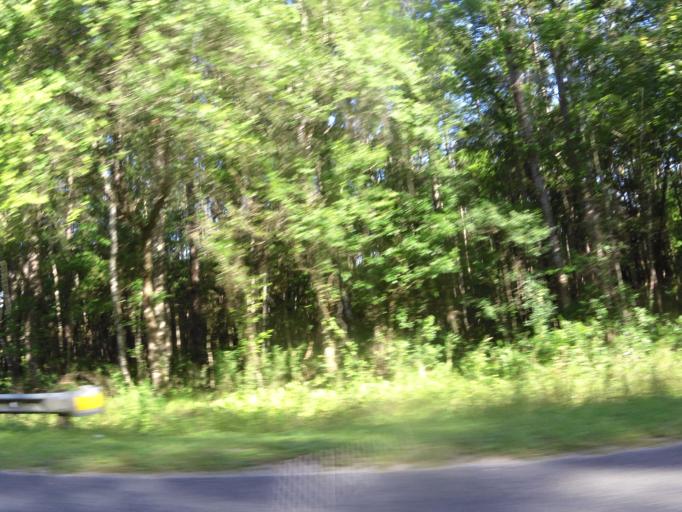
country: US
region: Florida
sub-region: Nassau County
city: Nassau Village-Ratliff
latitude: 30.4839
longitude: -81.8447
